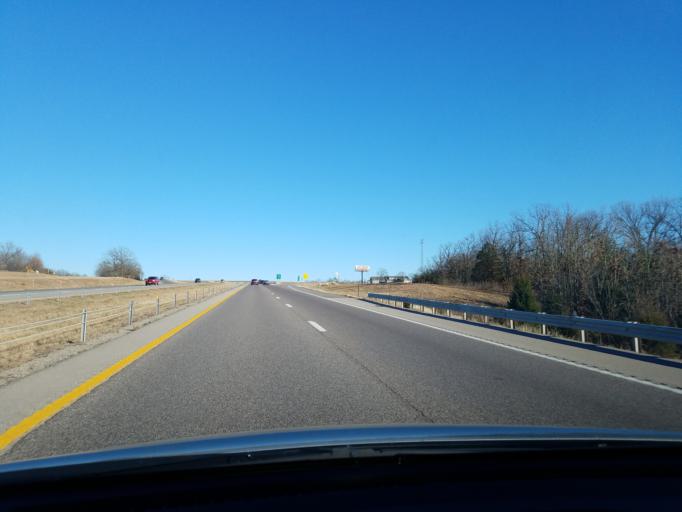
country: US
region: Missouri
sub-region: Phelps County
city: Rolla
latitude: 37.9451
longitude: -91.8898
